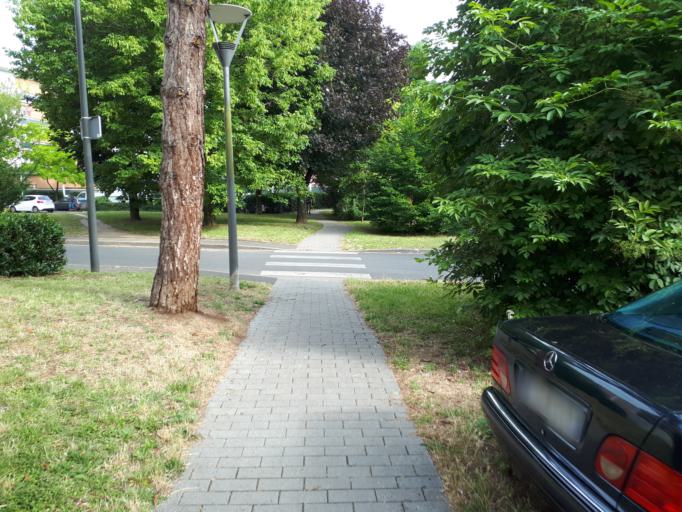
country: FR
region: Centre
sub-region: Departement d'Indre-et-Loire
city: Tours
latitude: 47.3820
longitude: 0.7009
